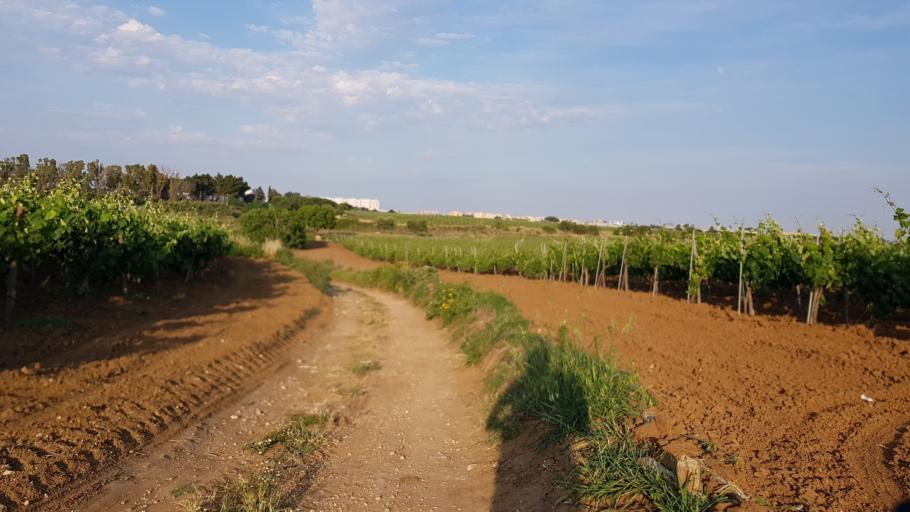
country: IT
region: Apulia
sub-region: Provincia di Brindisi
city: Brindisi
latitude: 40.6238
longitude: 17.8907
